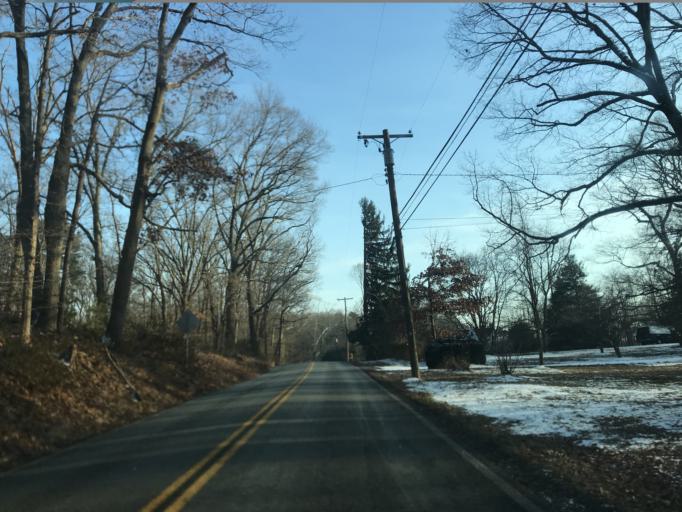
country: US
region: Maryland
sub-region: Harford County
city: Joppatowne
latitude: 39.4201
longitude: -76.3513
